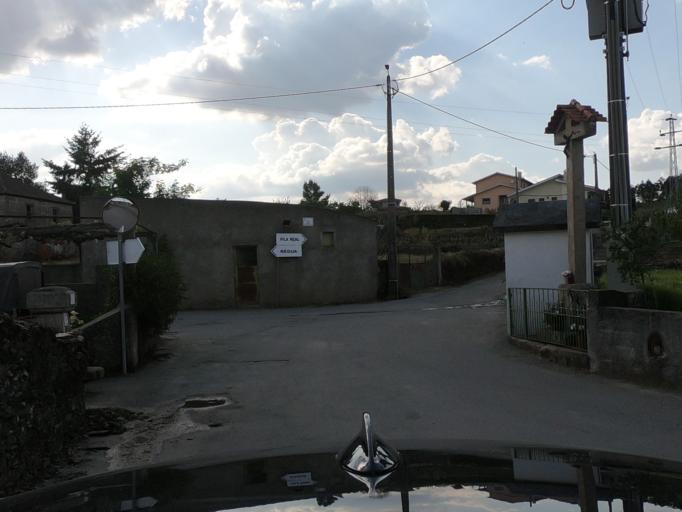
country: PT
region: Vila Real
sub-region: Sabrosa
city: Vilela
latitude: 41.2415
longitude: -7.6551
